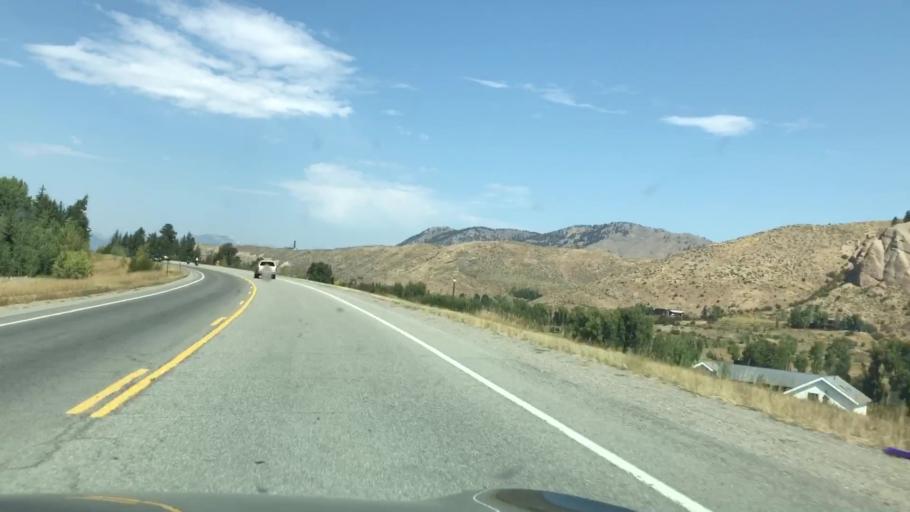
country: US
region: Wyoming
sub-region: Teton County
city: Hoback
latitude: 43.3556
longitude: -110.7210
